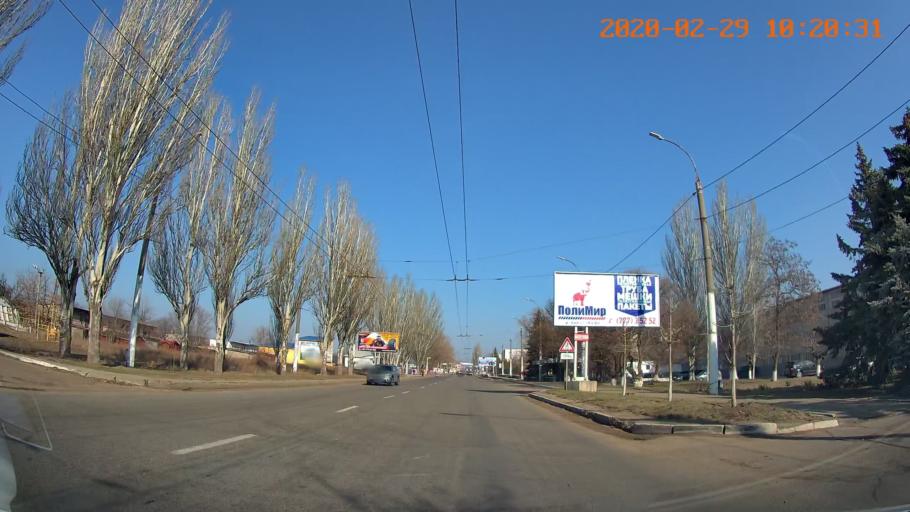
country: MD
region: Telenesti
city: Tiraspolul Nou
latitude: 46.8610
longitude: 29.6104
